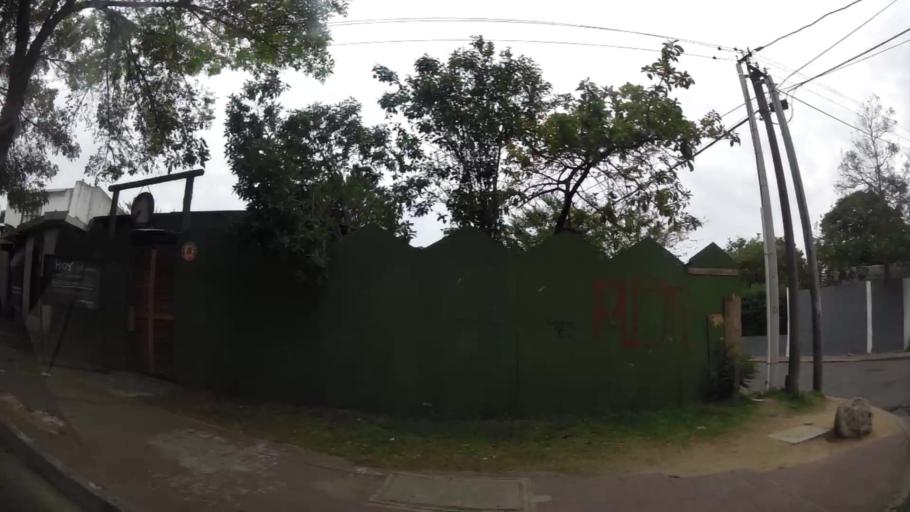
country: UY
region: Maldonado
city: Maldonado
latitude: -34.9018
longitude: -54.9664
